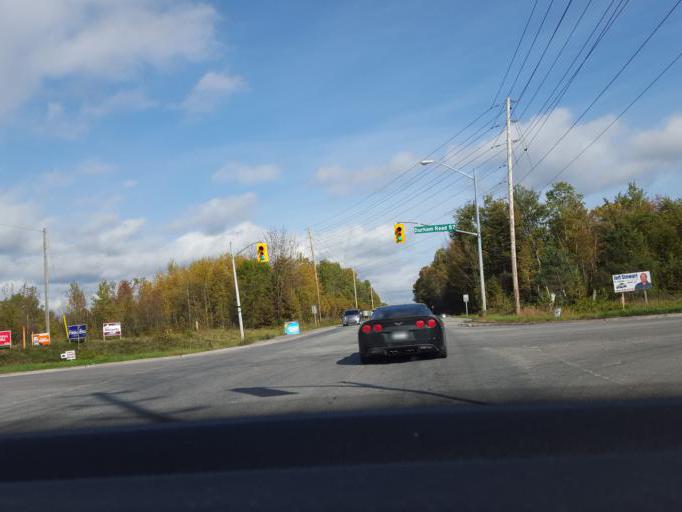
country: CA
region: Ontario
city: Oshawa
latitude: 43.9678
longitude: -78.7277
